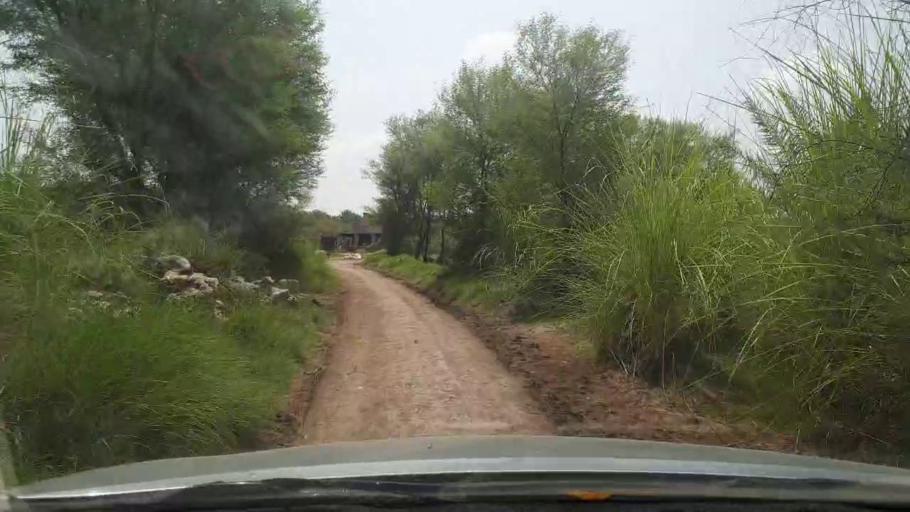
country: PK
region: Sindh
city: Khairpur
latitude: 27.4844
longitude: 68.7323
